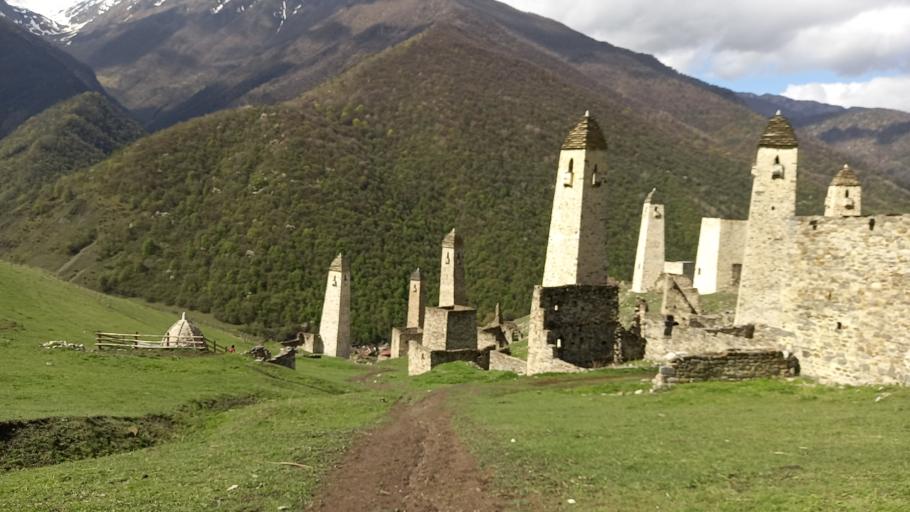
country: RU
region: Ingushetiya
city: Dzhayrakh
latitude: 42.8041
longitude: 44.7609
